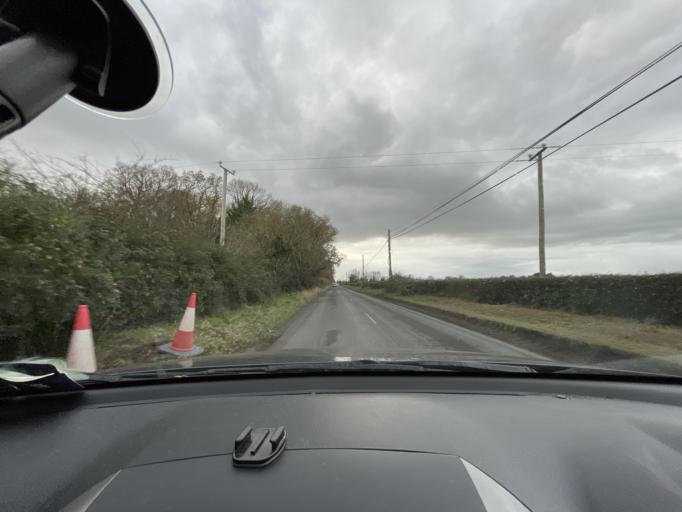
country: IE
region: Leinster
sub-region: Lu
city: Drogheda
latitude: 53.7370
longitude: -6.3092
